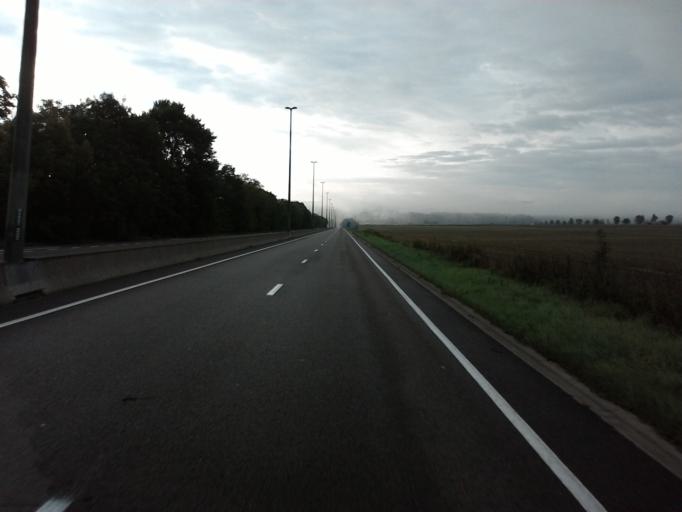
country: BE
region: Wallonia
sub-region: Province du Luxembourg
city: Attert
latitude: 49.7583
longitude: 5.7756
